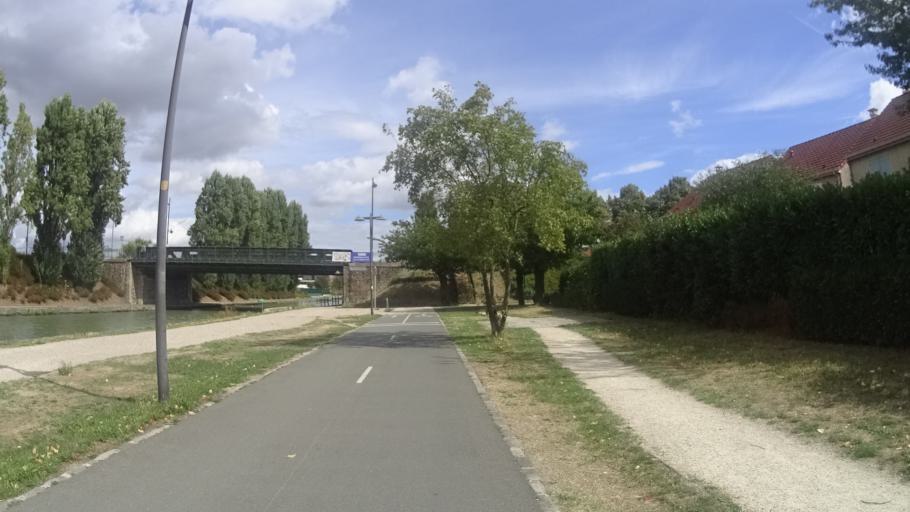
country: FR
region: Ile-de-France
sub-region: Departement de Seine-Saint-Denis
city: Les Pavillons-sous-Bois
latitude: 48.9140
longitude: 2.5019
